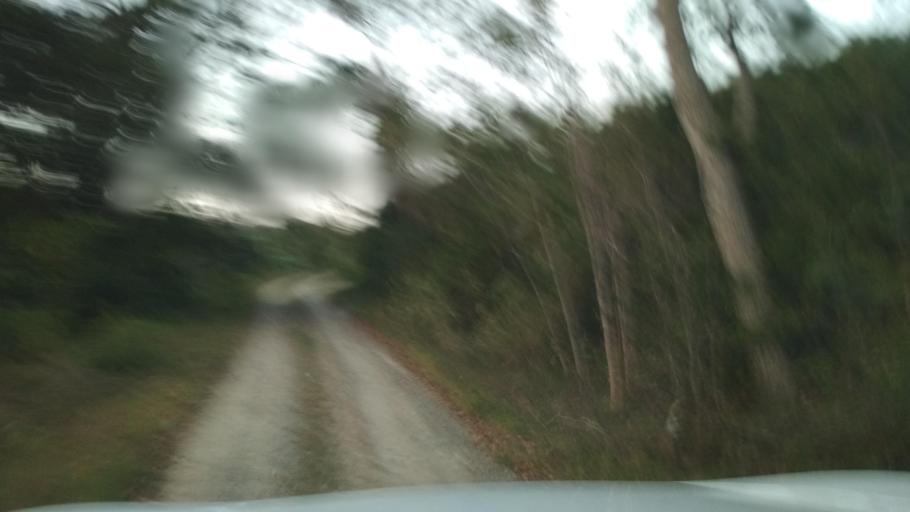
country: MX
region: Veracruz
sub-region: Poza Rica de Hidalgo
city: Arroyo del Maiz Uno
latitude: 20.4826
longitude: -97.3900
